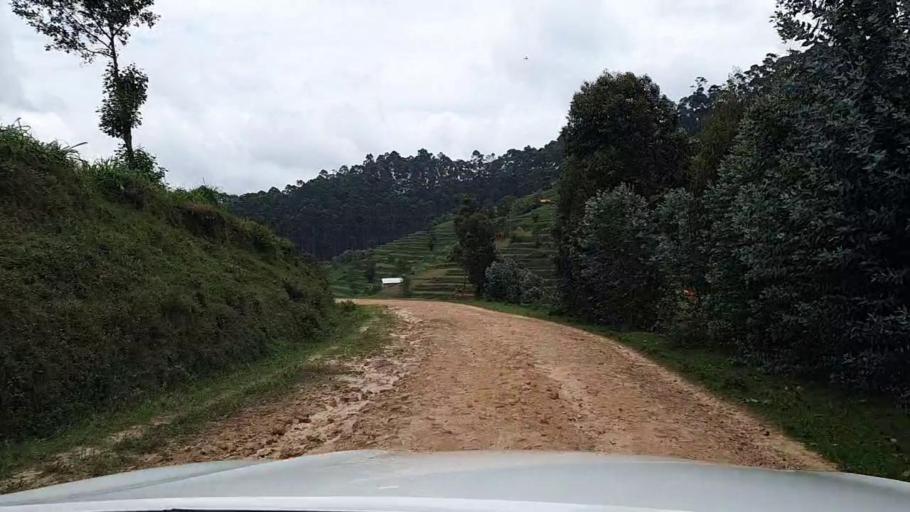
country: RW
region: Western Province
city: Kibuye
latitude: -2.2836
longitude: 29.3698
